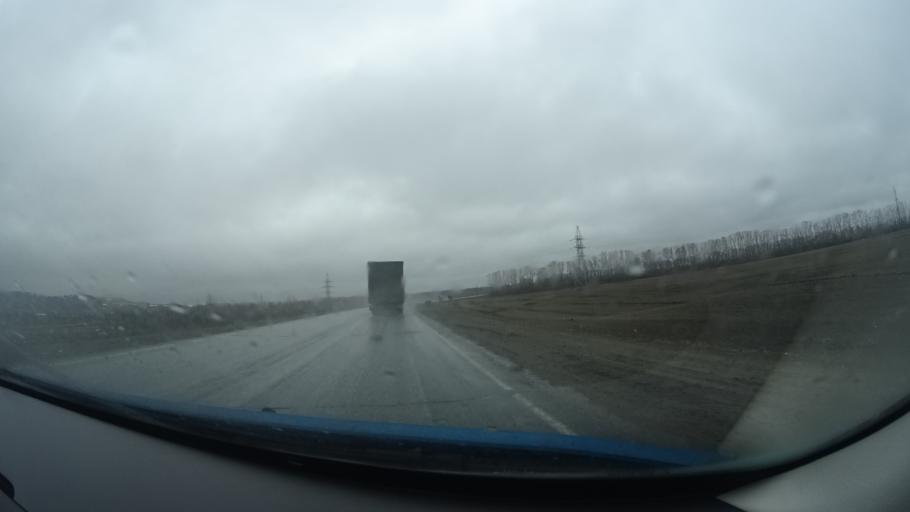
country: RU
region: Bashkortostan
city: Kandry
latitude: 54.5698
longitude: 54.2245
